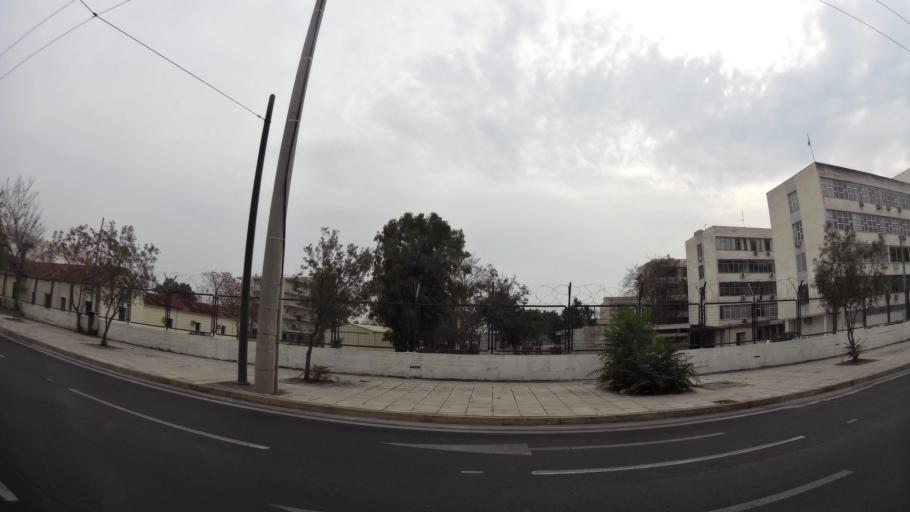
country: GR
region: Attica
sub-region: Nomarchia Athinas
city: Tavros
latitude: 37.9754
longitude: 23.7025
